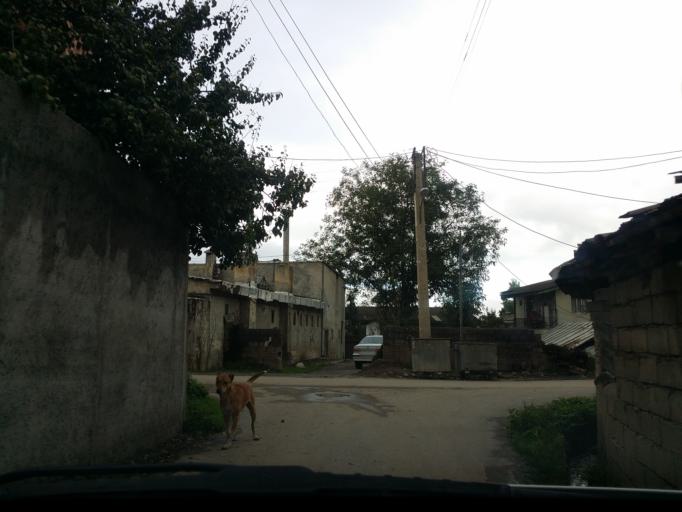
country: IR
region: Mazandaran
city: `Abbasabad
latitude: 36.5050
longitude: 51.1887
